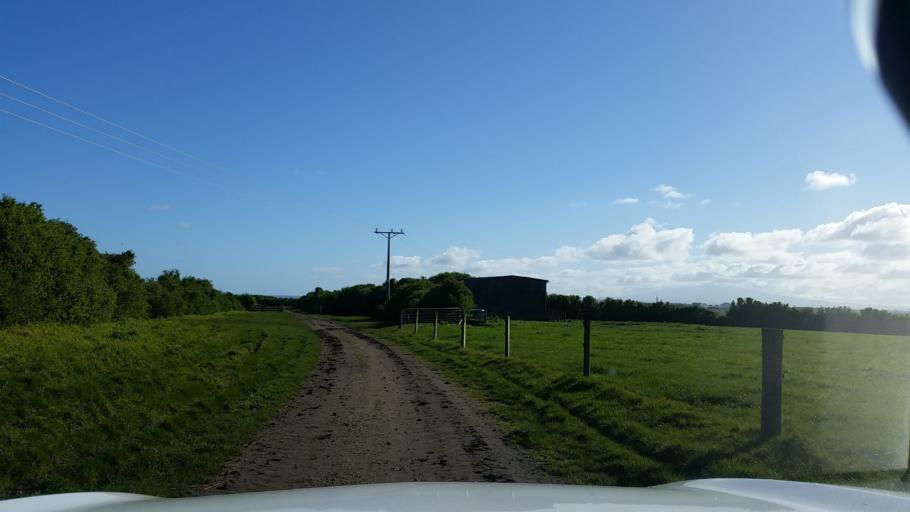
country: NZ
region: Taranaki
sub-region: South Taranaki District
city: Hawera
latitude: -39.6599
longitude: 174.3621
